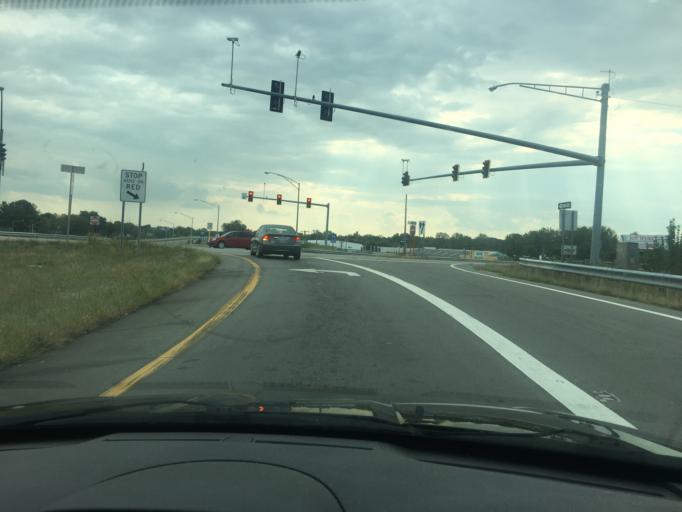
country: US
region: Ohio
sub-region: Clark County
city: Springfield
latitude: 39.9438
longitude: -83.8424
